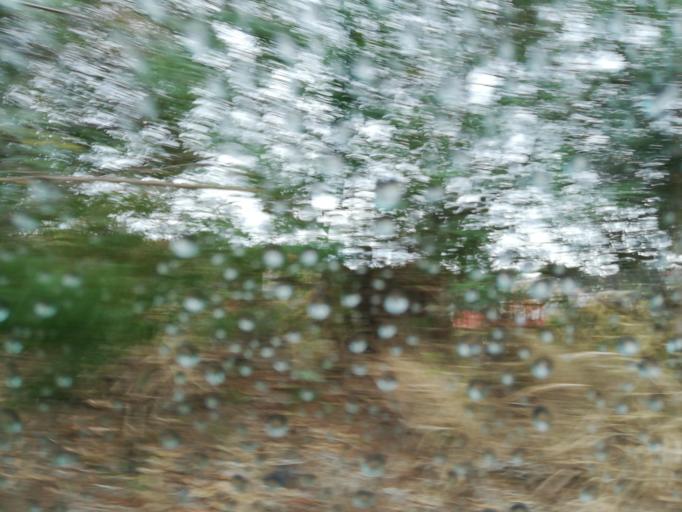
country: MU
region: Black River
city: Petite Riviere
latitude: -20.2106
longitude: 57.4673
